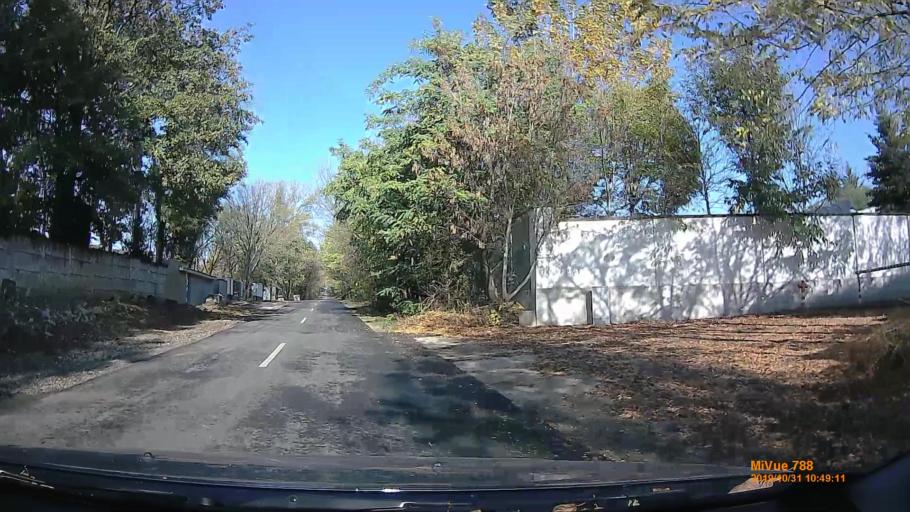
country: HU
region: Pest
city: Urom
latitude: 47.5891
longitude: 19.0055
